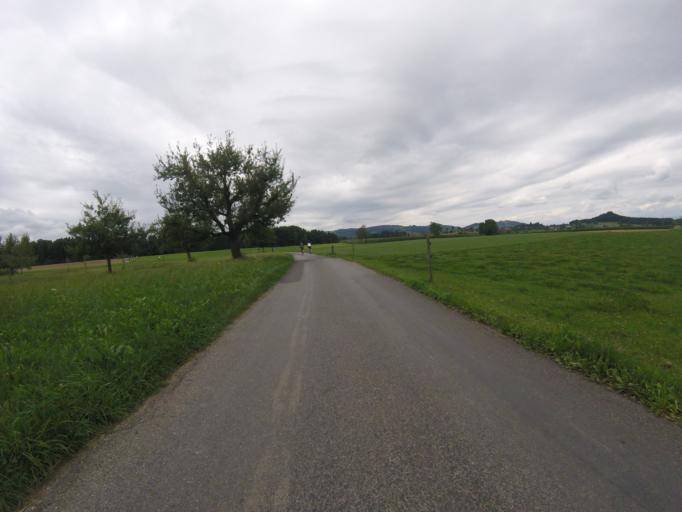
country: CH
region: Bern
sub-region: Bern-Mittelland District
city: Rubigen
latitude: 46.9139
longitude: 7.5476
